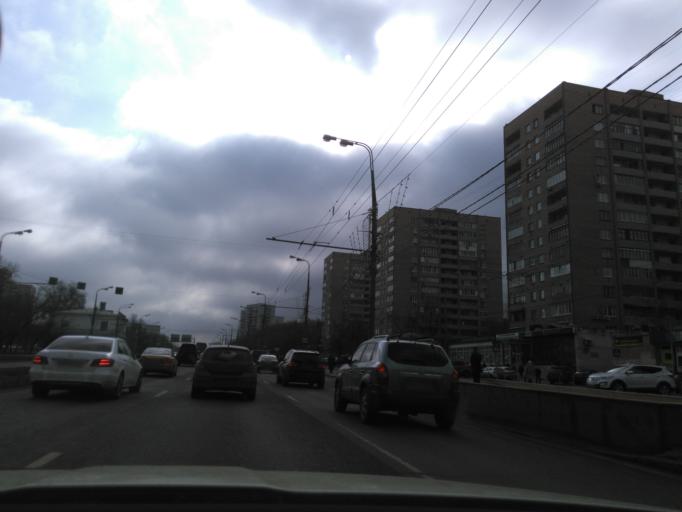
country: RU
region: Moscow
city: Pokrovskoye-Streshnevo
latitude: 55.8170
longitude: 37.4604
